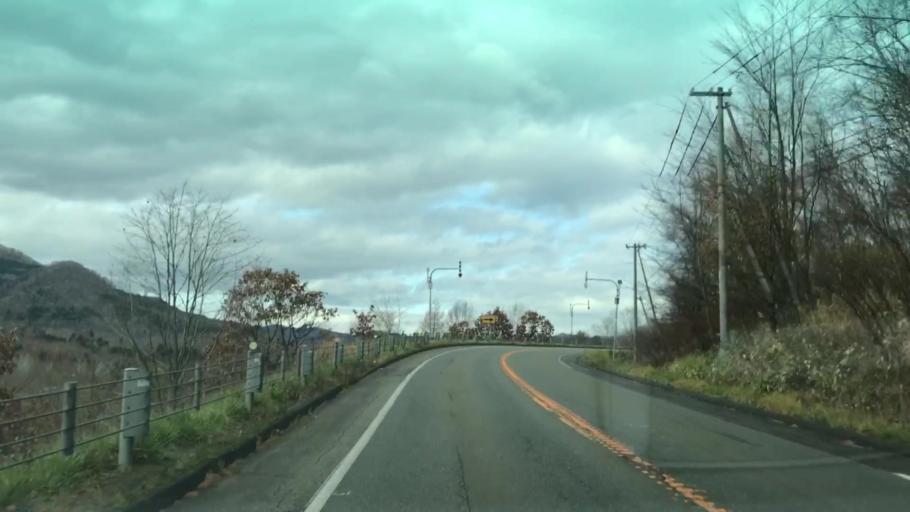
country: JP
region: Hokkaido
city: Shimo-furano
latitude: 42.8853
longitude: 142.4337
